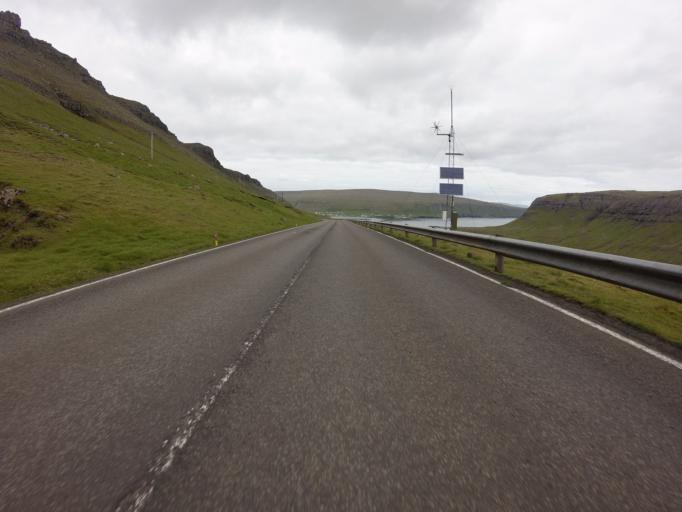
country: FO
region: Suduroy
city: Tvoroyri
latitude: 61.5755
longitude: -6.9373
